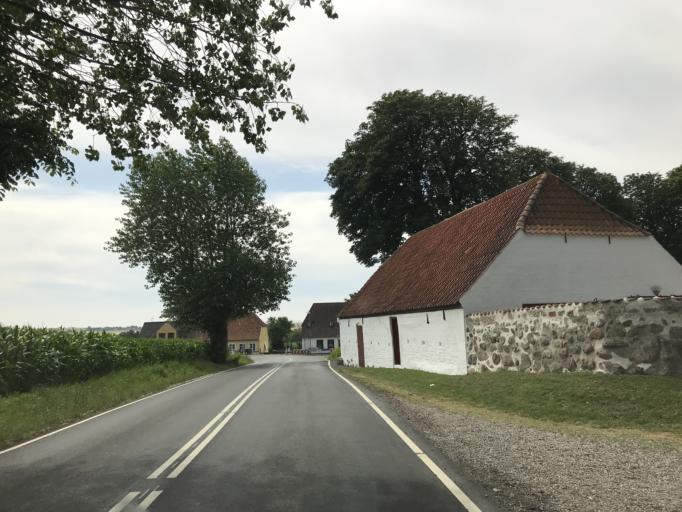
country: DK
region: South Denmark
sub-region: AEro Kommune
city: AEroskobing
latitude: 54.8543
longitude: 10.4007
